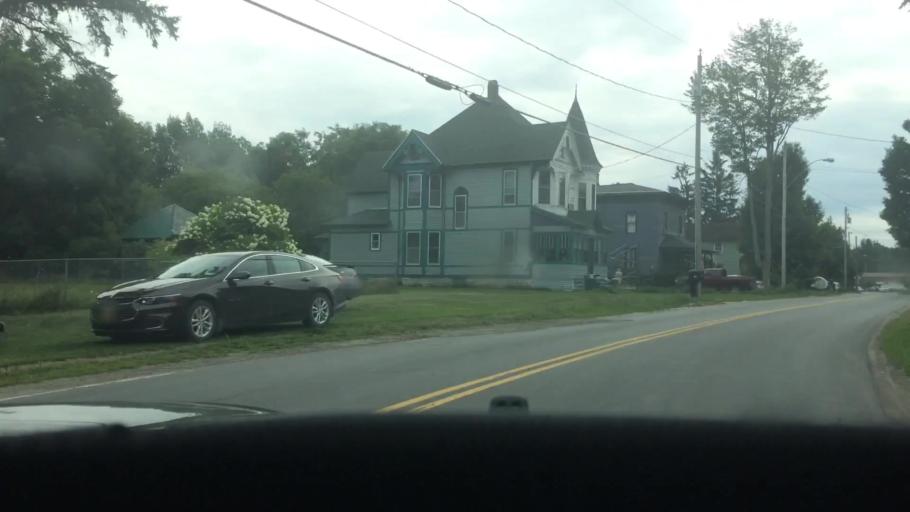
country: US
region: New York
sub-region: St. Lawrence County
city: Canton
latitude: 44.5073
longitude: -75.2760
